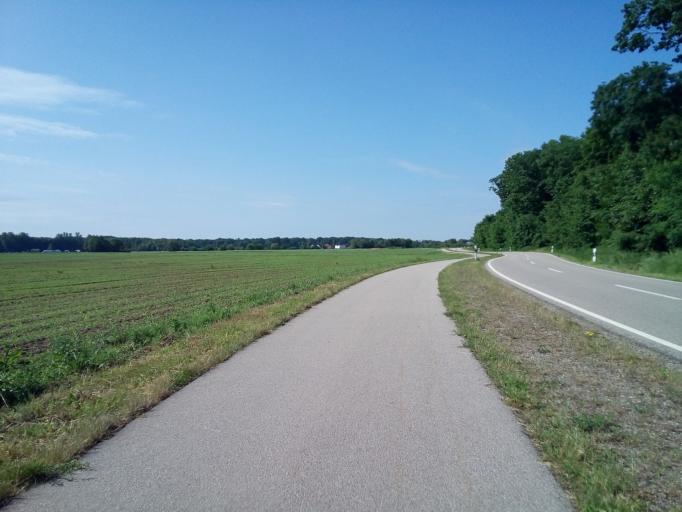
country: DE
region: Baden-Wuerttemberg
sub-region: Freiburg Region
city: Rheinau
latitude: 48.6168
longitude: 7.9133
